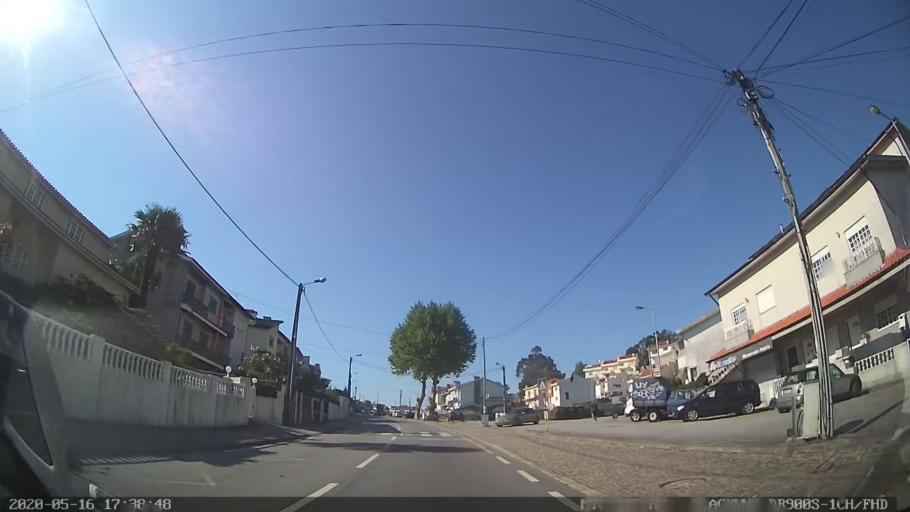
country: PT
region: Porto
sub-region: Valongo
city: Valongo
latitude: 41.1874
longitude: -8.5248
